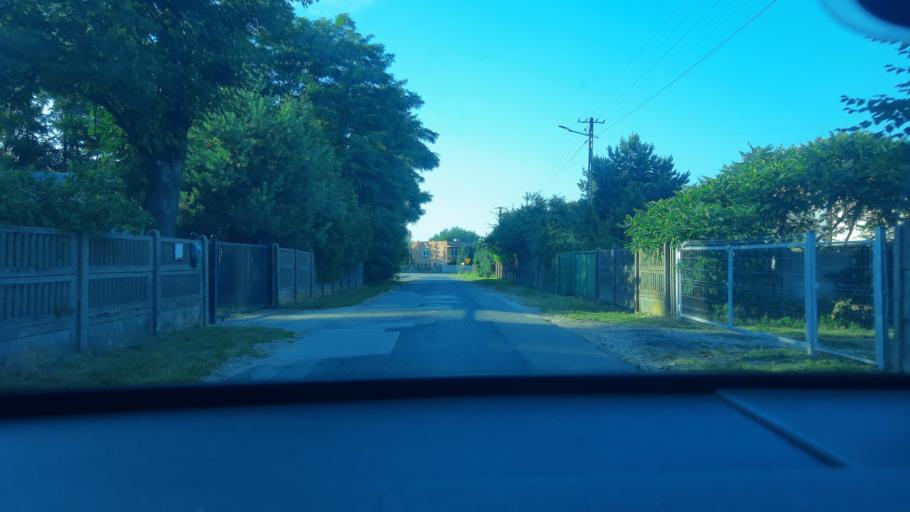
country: PL
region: Lodz Voivodeship
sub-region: Powiat sieradzki
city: Sieradz
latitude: 51.5461
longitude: 18.7548
